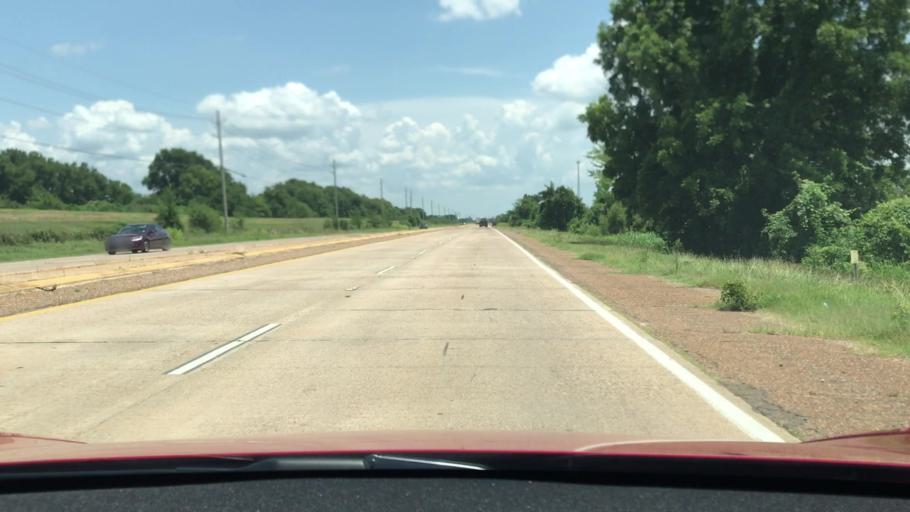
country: US
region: Louisiana
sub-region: Bossier Parish
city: Bossier City
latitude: 32.3873
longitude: -93.6782
